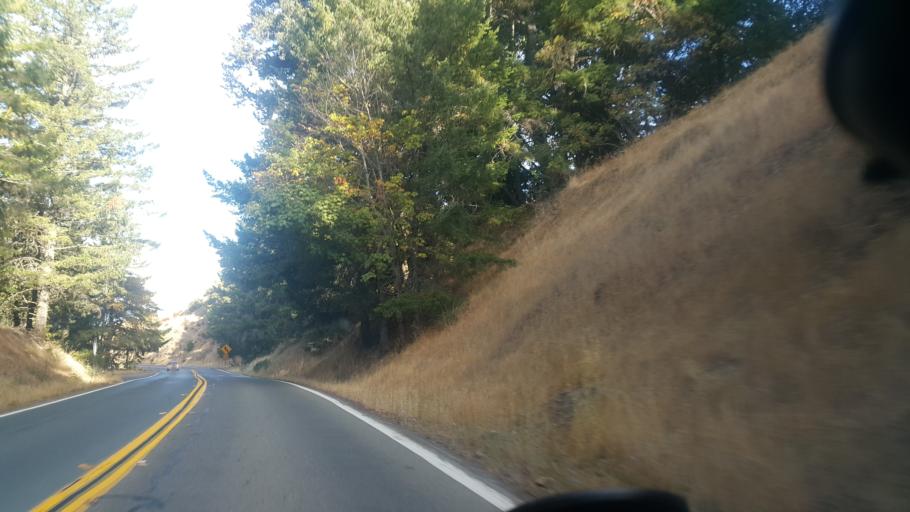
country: US
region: California
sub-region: Mendocino County
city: Brooktrails
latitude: 39.3896
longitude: -123.4436
